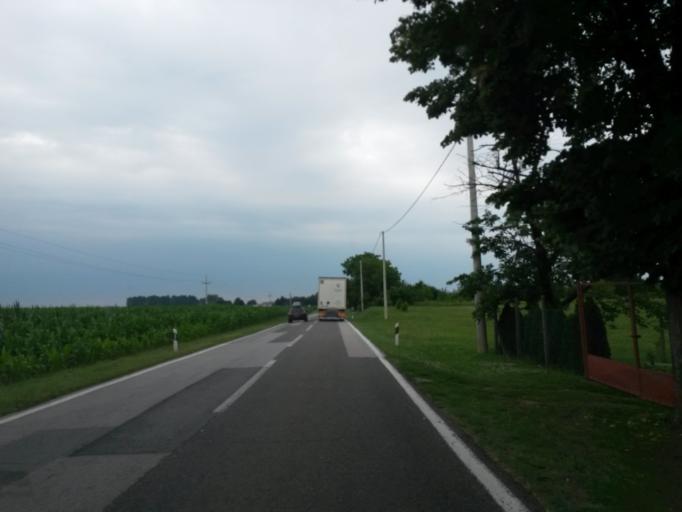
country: HR
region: Vukovarsko-Srijemska
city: Lovas
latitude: 45.2850
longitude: 19.1218
